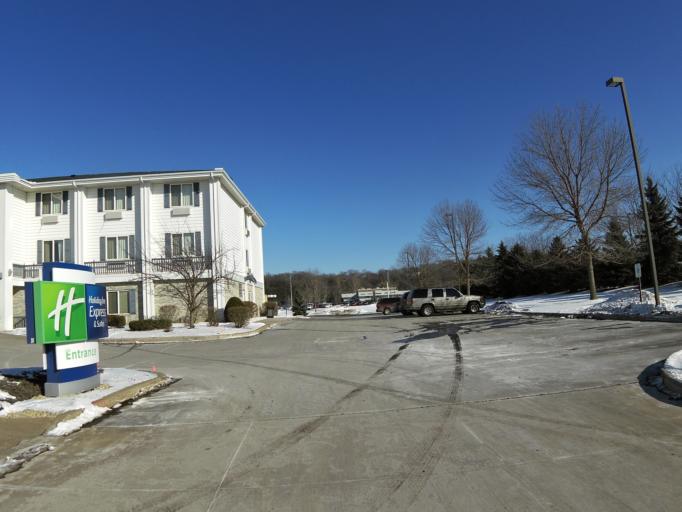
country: US
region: Wisconsin
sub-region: Saint Croix County
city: Hudson
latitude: 44.9576
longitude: -92.7232
